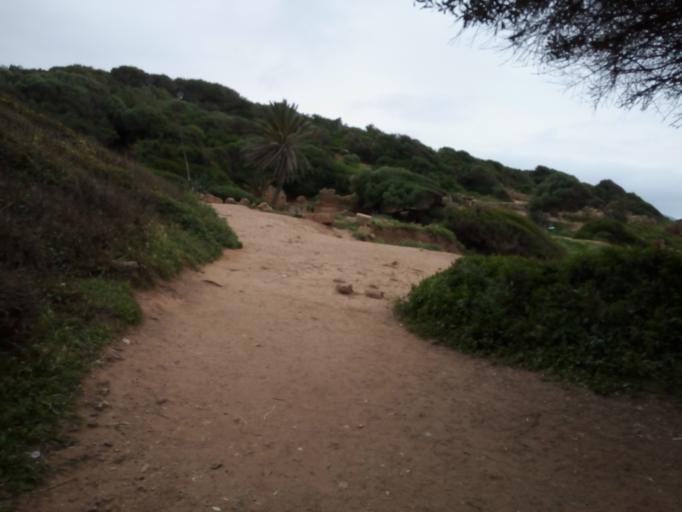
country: DZ
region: Tipaza
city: Tipasa
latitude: 36.5943
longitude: 2.4430
